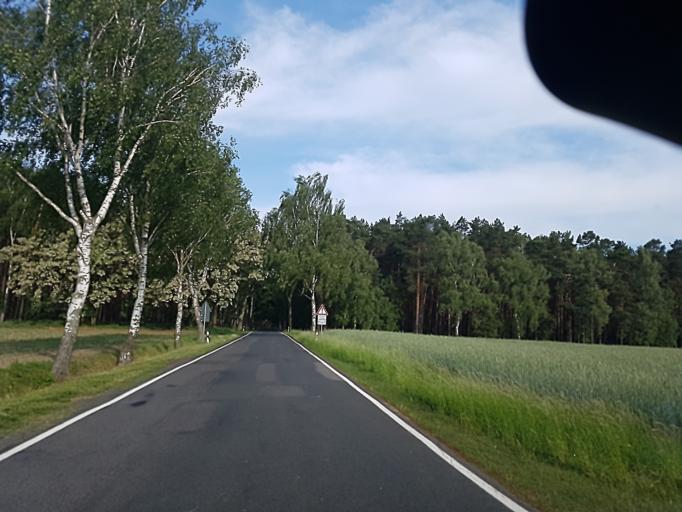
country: DE
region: Brandenburg
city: Belzig
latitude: 52.0650
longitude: 12.5712
